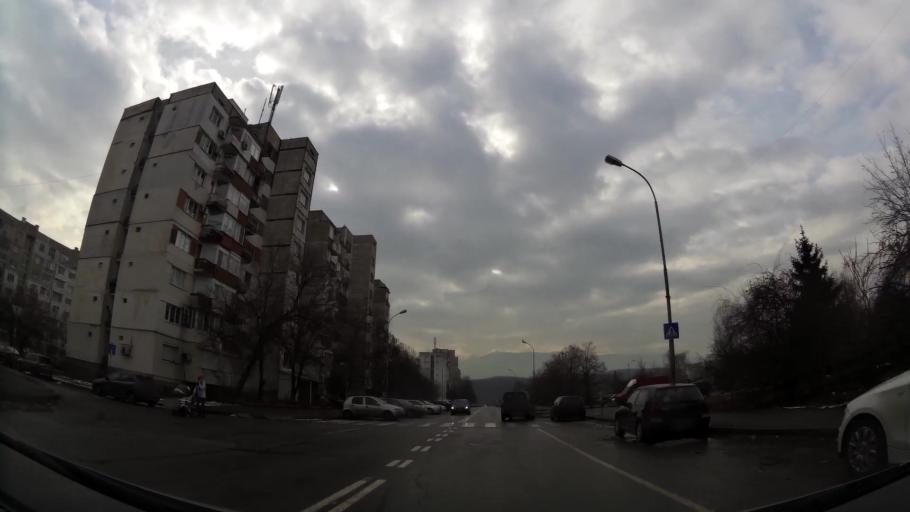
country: BG
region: Sofia-Capital
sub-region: Stolichna Obshtina
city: Sofia
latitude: 42.7134
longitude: 23.2584
